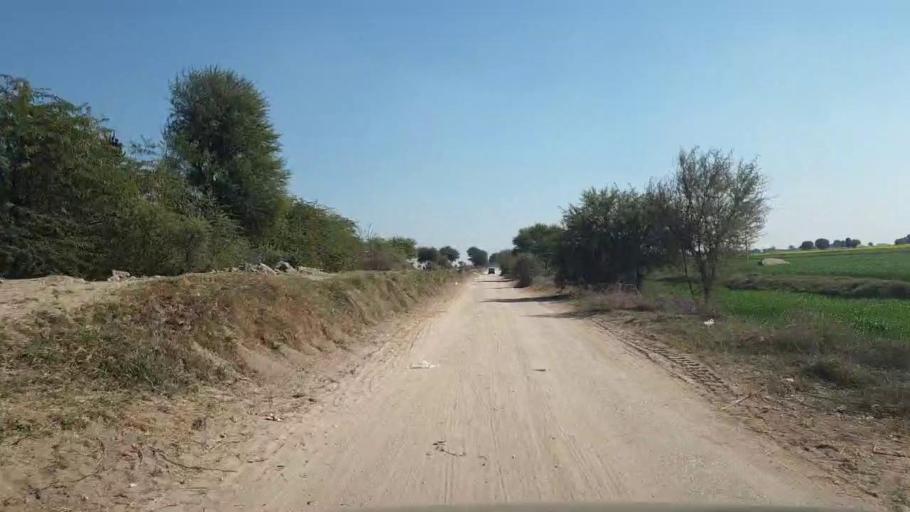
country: PK
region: Sindh
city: Shahpur Chakar
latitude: 26.1439
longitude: 68.6505
